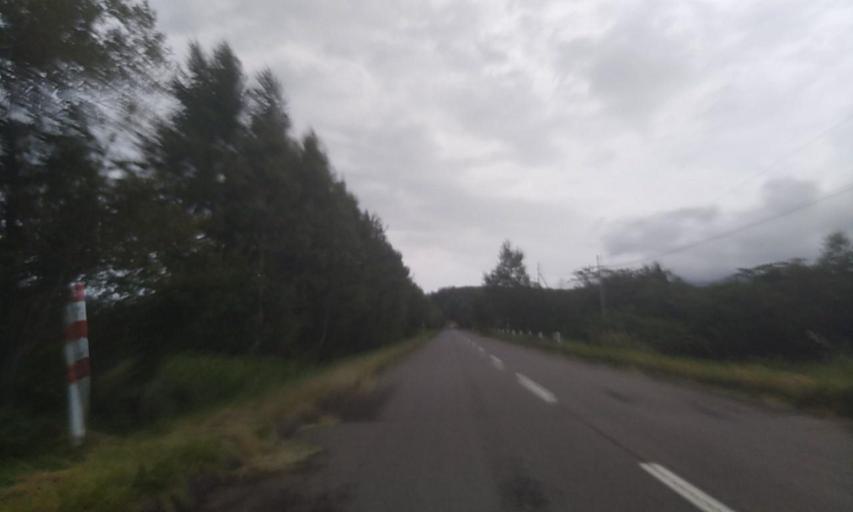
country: JP
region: Hokkaido
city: Shibetsu
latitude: 43.9066
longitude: 144.7941
